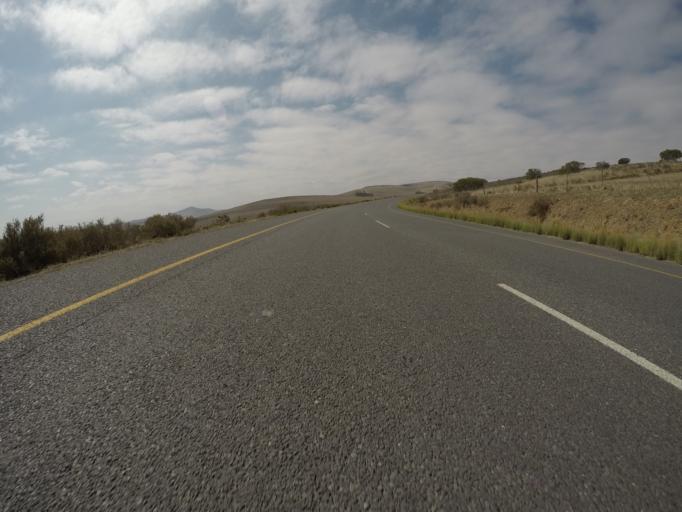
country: ZA
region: Western Cape
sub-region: City of Cape Town
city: Sunset Beach
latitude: -33.7909
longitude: 18.5713
